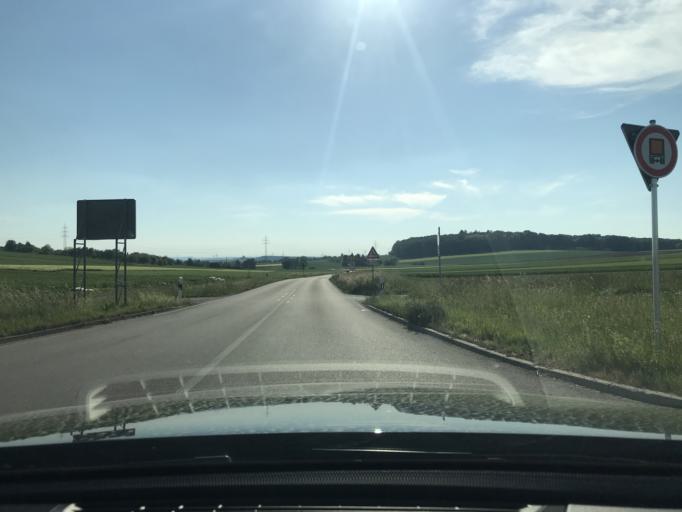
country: DE
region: Baden-Wuerttemberg
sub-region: Regierungsbezirk Stuttgart
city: Schwaikheim
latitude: 48.8931
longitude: 9.3600
